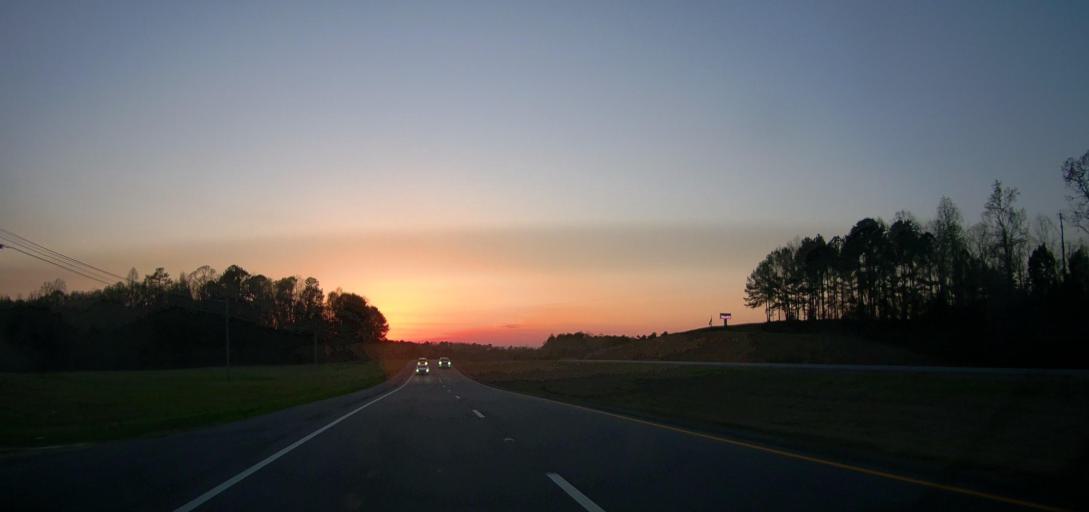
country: US
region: Alabama
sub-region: Tallapoosa County
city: Alexander City
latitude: 32.8855
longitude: -85.8653
